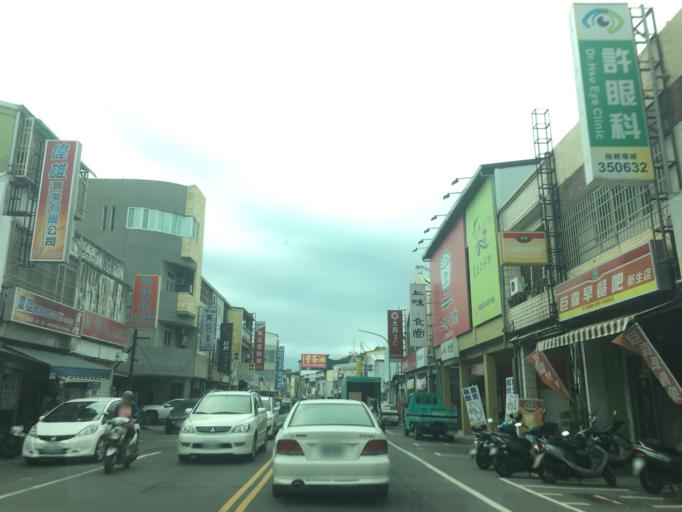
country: TW
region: Taiwan
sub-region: Taitung
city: Taitung
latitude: 22.7600
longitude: 121.1394
